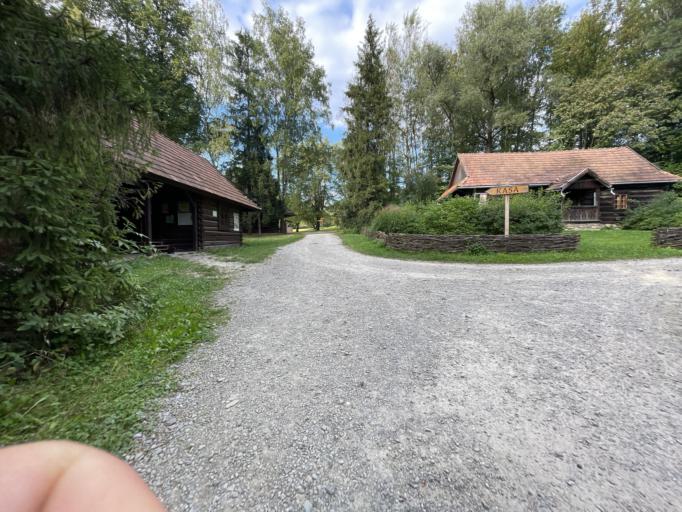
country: PL
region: Lesser Poland Voivodeship
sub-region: Powiat nowosadecki
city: Nowy Sacz
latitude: 49.6152
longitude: 20.7334
